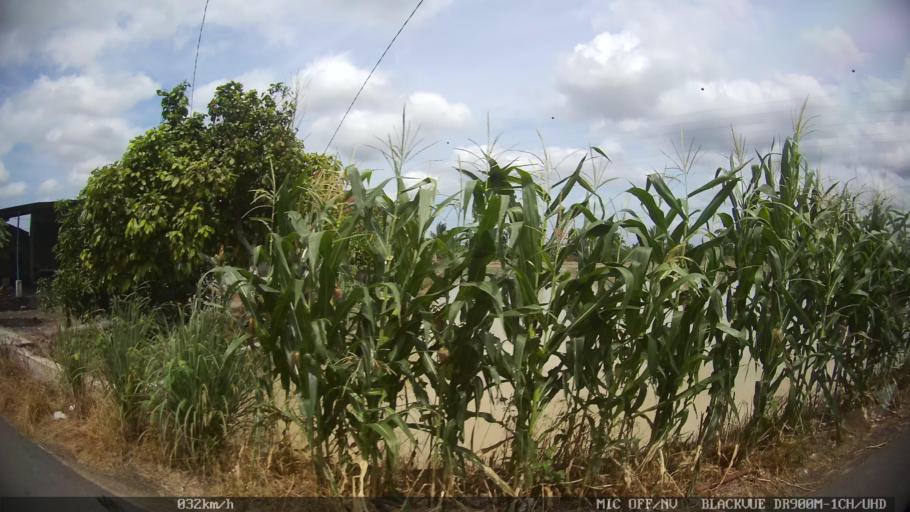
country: ID
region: North Sumatra
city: Percut
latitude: 3.5749
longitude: 98.8408
